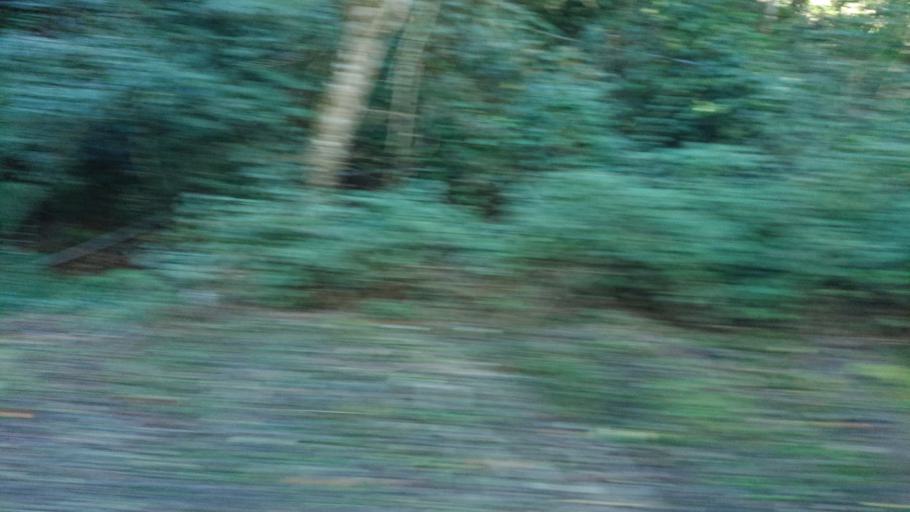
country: TW
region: Taiwan
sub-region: Hualien
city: Hualian
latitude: 24.3492
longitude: 121.3242
